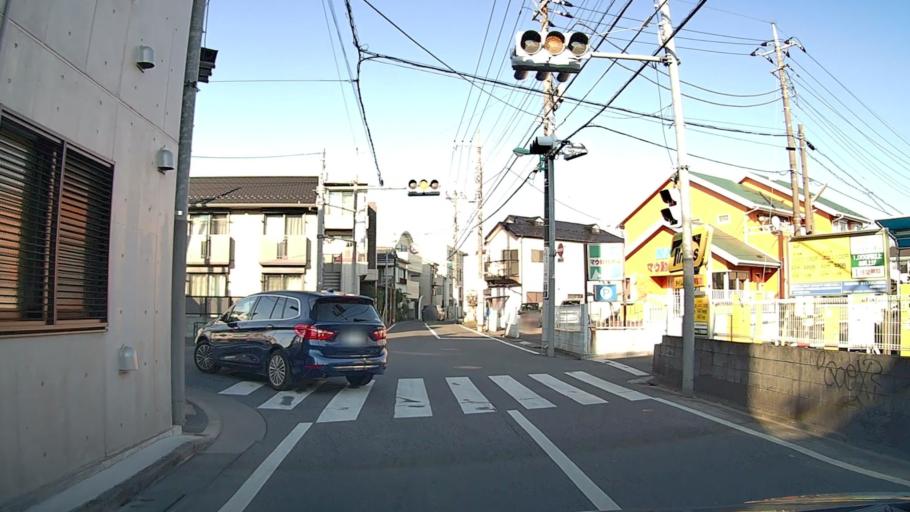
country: JP
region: Saitama
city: Wako
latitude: 35.7480
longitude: 139.6496
